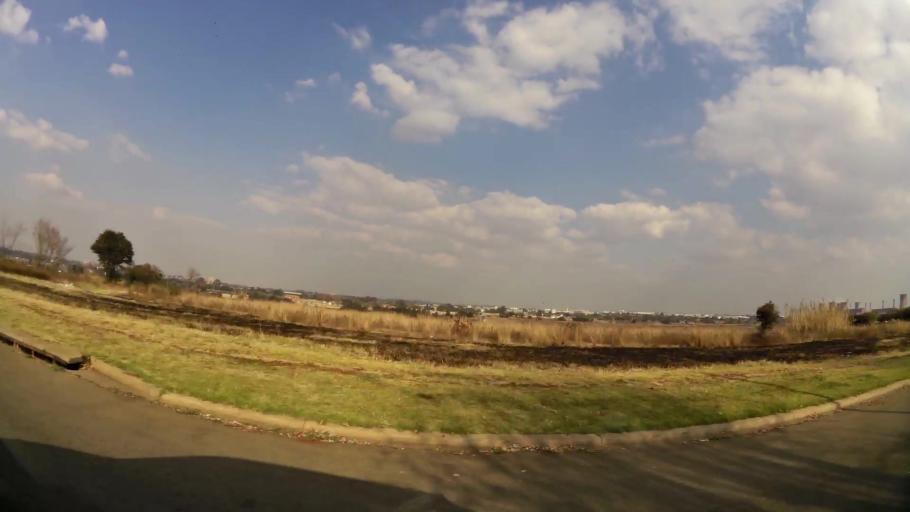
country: ZA
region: Gauteng
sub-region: City of Johannesburg Metropolitan Municipality
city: Modderfontein
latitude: -26.0979
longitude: 28.2037
